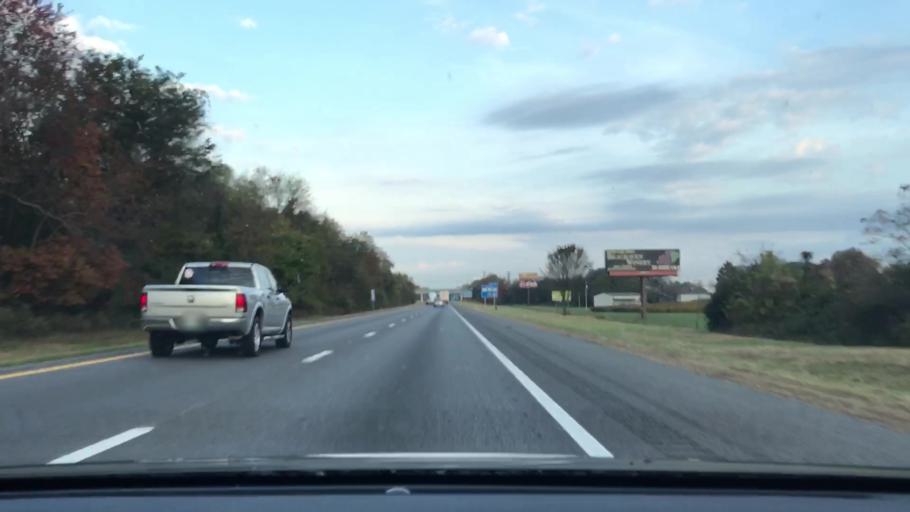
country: US
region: Tennessee
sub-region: Montgomery County
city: Clarksville
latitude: 36.5752
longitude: -87.2602
